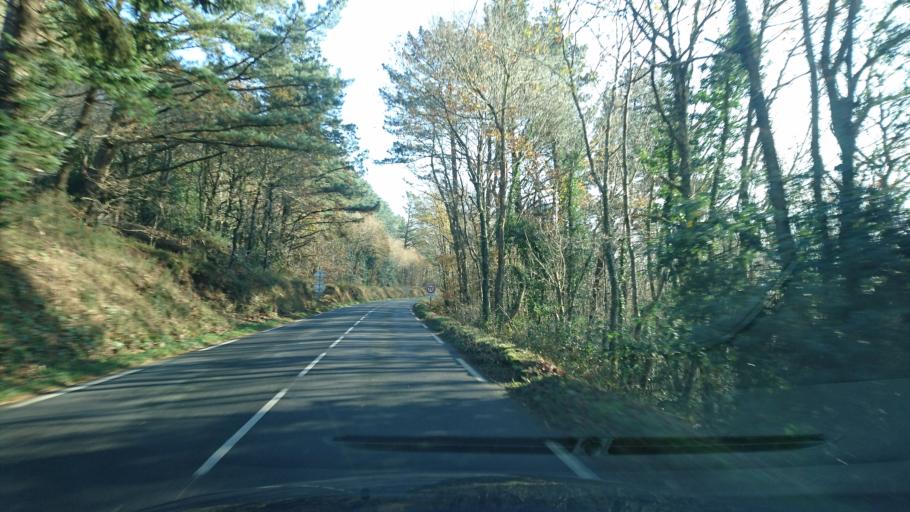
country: FR
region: Brittany
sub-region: Departement du Finistere
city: Logonna-Daoulas
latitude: 48.2750
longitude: -4.2696
